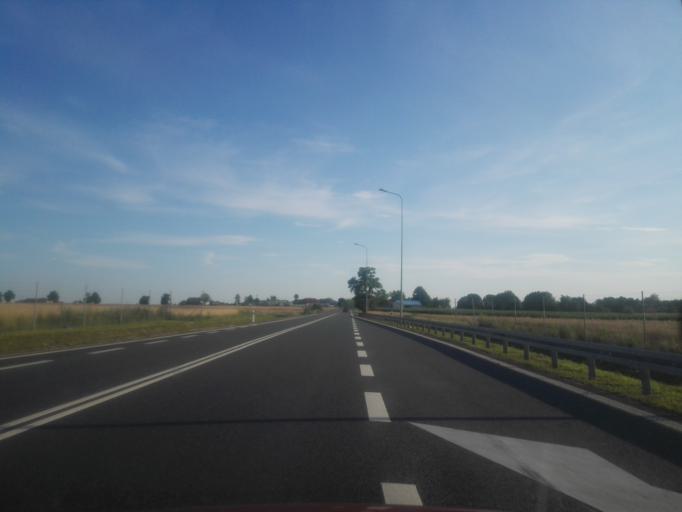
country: PL
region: Lodz Voivodeship
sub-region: Powiat wieruszowski
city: Walichnowy
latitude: 51.3124
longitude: 18.3840
